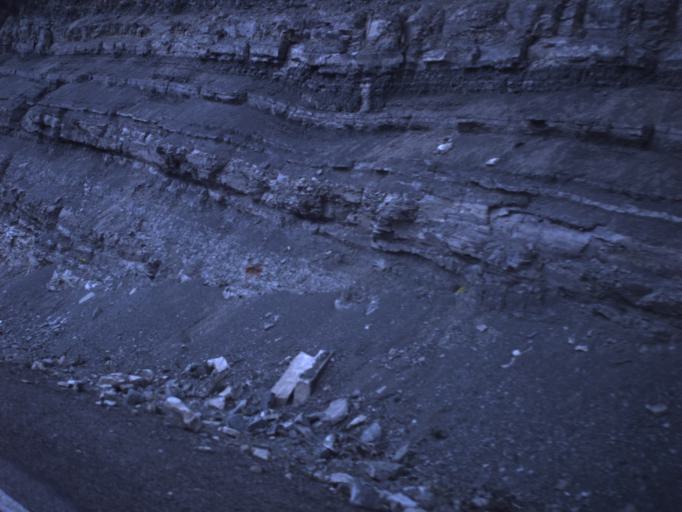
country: US
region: Utah
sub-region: Carbon County
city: Helper
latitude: 39.8727
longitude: -110.7626
